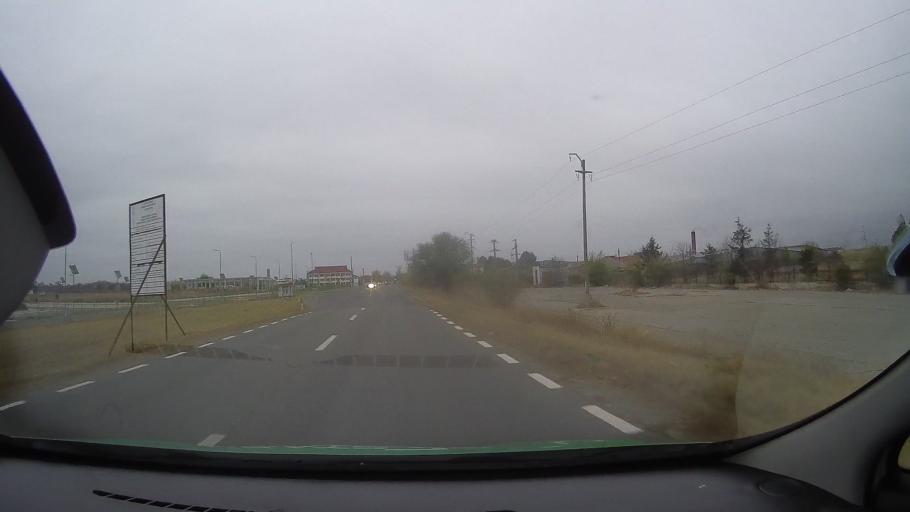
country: RO
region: Ialomita
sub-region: Comuna Slobozia
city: Slobozia
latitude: 44.5822
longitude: 27.3881
